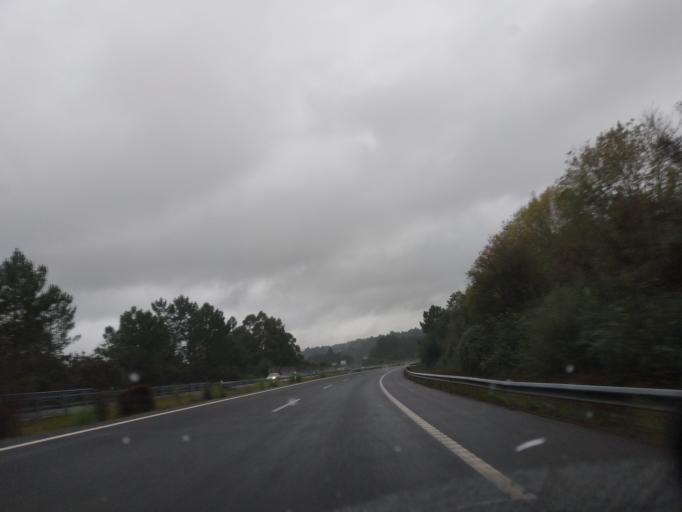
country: ES
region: Galicia
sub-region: Provincia da Coruna
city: Cambre
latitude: 43.2727
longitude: -8.3613
